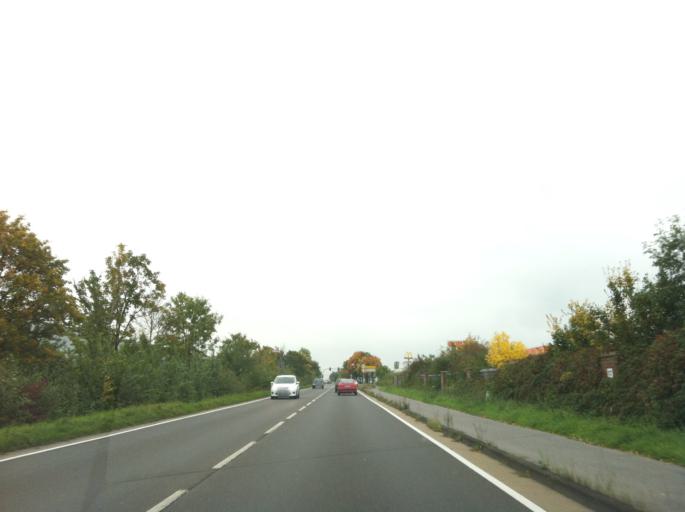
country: DE
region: North Rhine-Westphalia
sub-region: Regierungsbezirk Koln
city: Dueren
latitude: 50.7838
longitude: 6.5071
